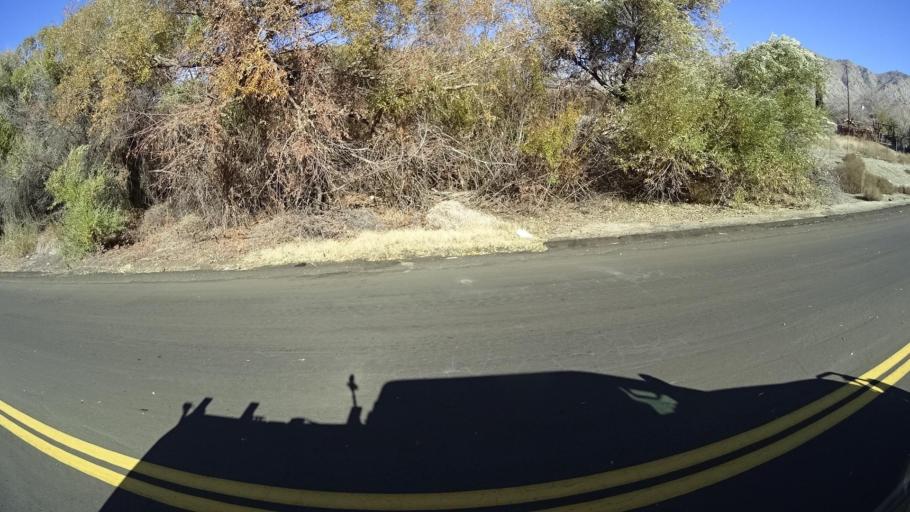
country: US
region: California
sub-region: Kern County
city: Lake Isabella
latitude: 35.6102
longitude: -118.4877
